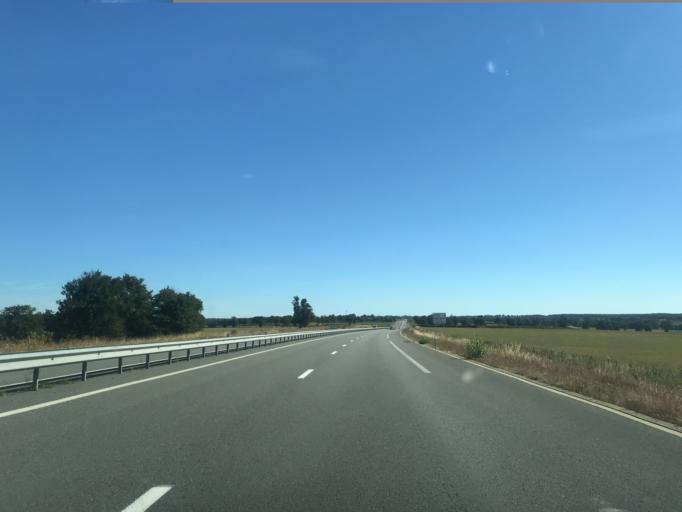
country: FR
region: Limousin
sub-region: Departement de la Creuse
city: Chambon-sur-Voueize
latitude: 46.2627
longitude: 2.3664
